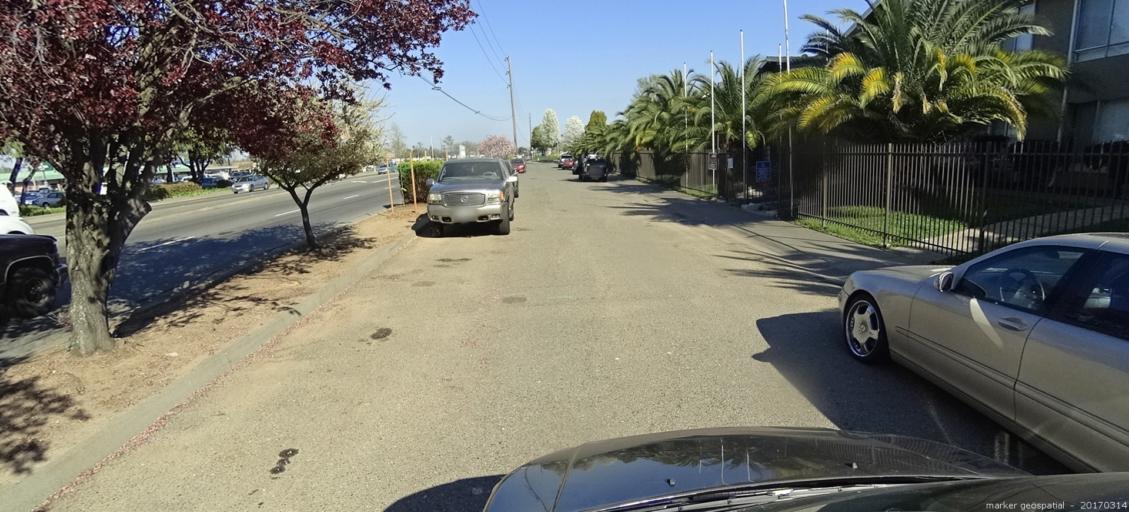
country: US
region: California
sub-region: Sacramento County
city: Parkway
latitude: 38.4954
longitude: -121.5106
